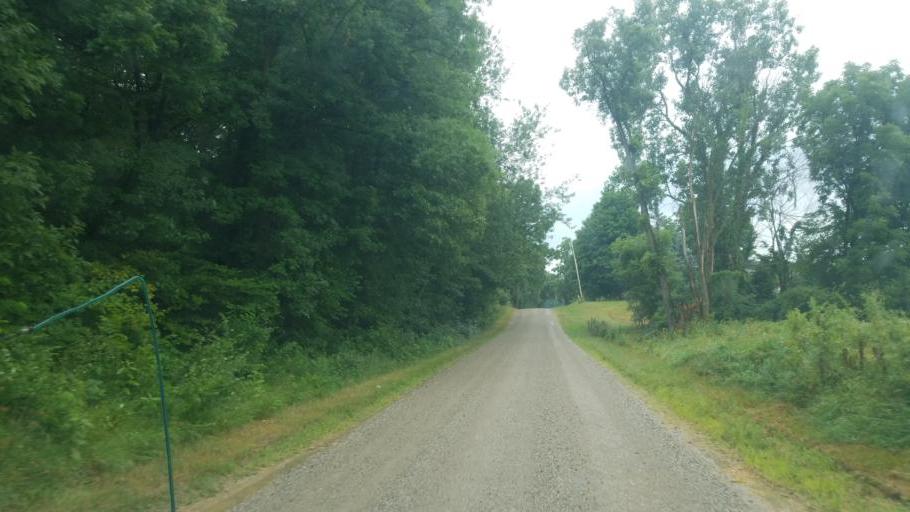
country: US
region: Indiana
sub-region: Steuben County
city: Hamilton
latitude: 41.5217
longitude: -84.9311
